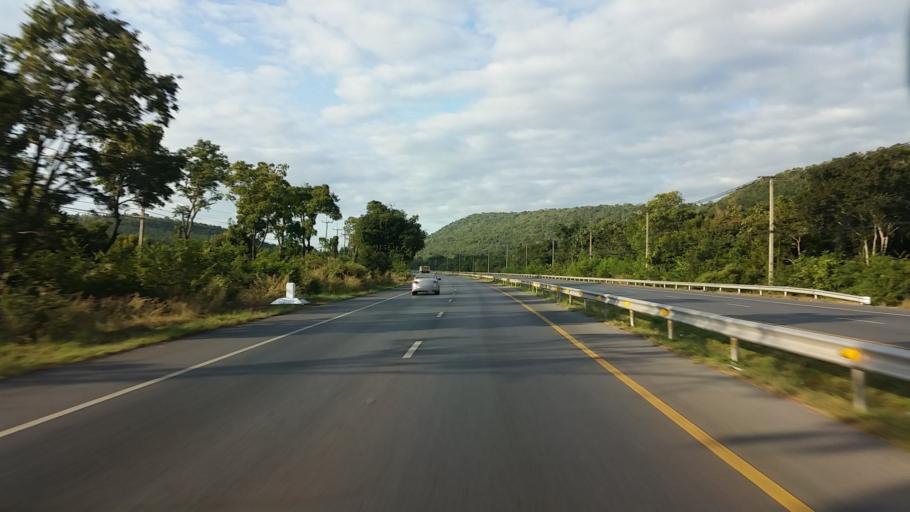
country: TH
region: Lop Buri
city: Phatthana Nikhom
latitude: 14.9778
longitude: 100.9068
